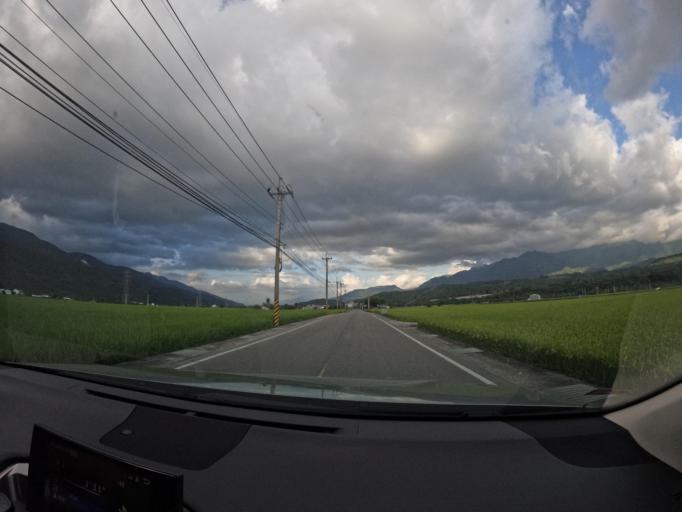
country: TW
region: Taiwan
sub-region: Taitung
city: Taitung
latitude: 23.1517
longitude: 121.2313
